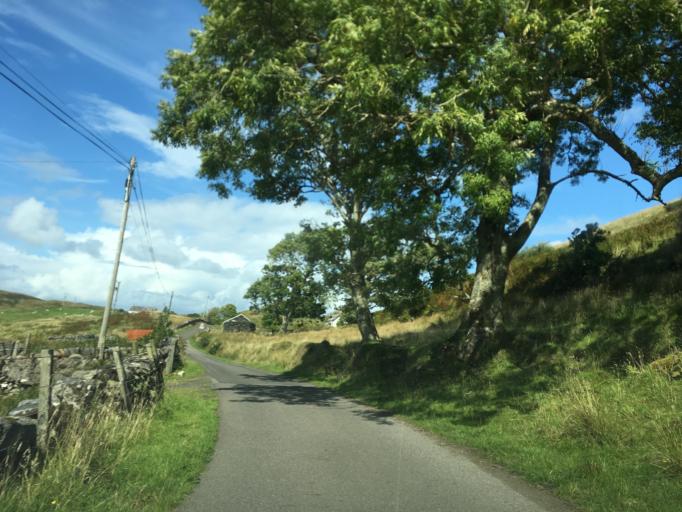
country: GB
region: Scotland
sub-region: Argyll and Bute
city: Oban
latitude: 56.2276
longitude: -5.6422
